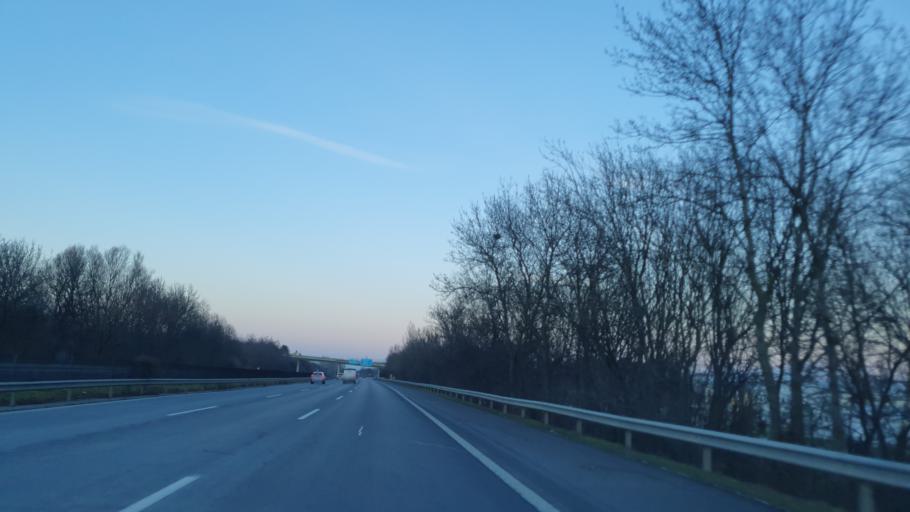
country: HU
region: Fejer
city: Kapolnasnyek
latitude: 47.2552
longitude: 18.6662
